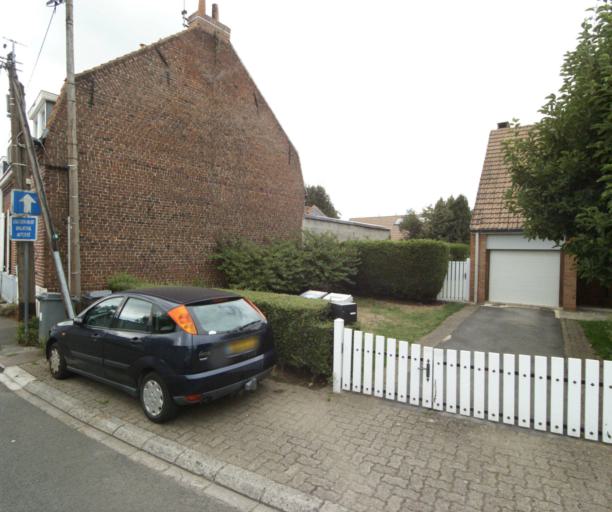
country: FR
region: Nord-Pas-de-Calais
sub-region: Departement du Nord
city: Mons-en-Baroeul
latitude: 50.6287
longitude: 3.1426
